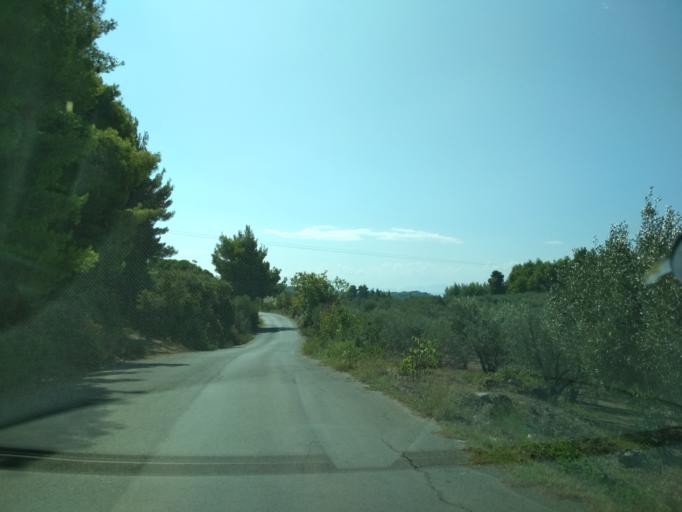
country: GR
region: Central Greece
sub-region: Nomos Evvoias
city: Roviai
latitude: 38.8247
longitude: 23.2455
